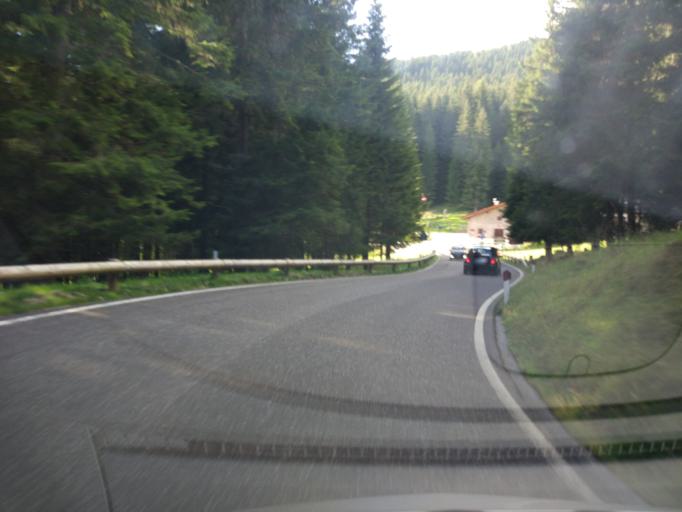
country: IT
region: Trentino-Alto Adige
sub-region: Provincia di Trento
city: Moena
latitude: 46.3089
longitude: 11.7492
